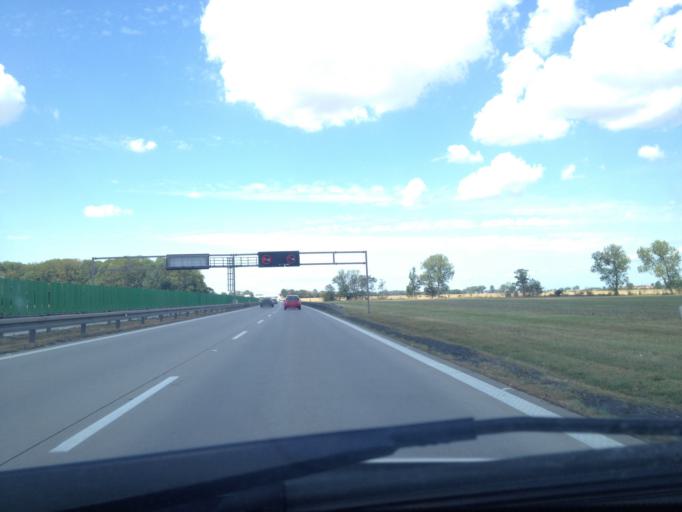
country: PL
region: Lower Silesian Voivodeship
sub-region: Powiat sredzki
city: Ciechow
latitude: 51.0462
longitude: 16.5826
